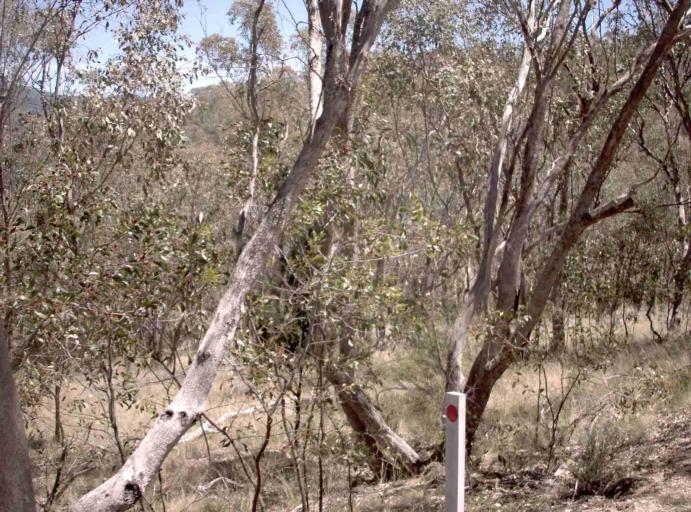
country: AU
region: New South Wales
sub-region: Snowy River
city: Jindabyne
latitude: -36.9433
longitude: 148.3400
